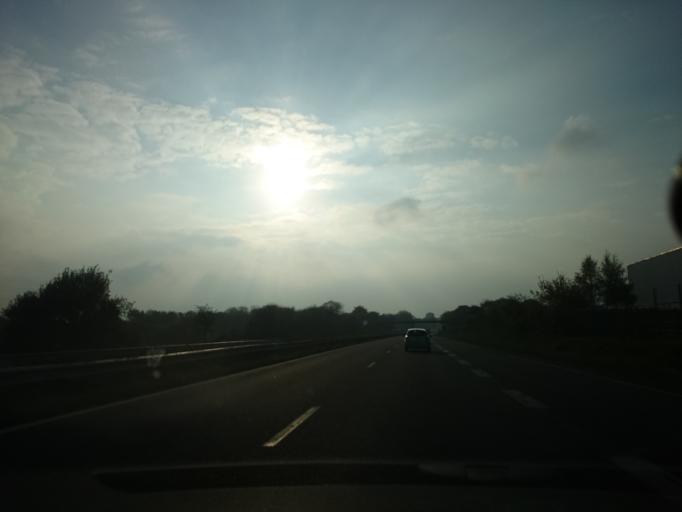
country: FR
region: Brittany
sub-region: Departement du Finistere
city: Bannalec
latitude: 47.8863
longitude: -3.6963
